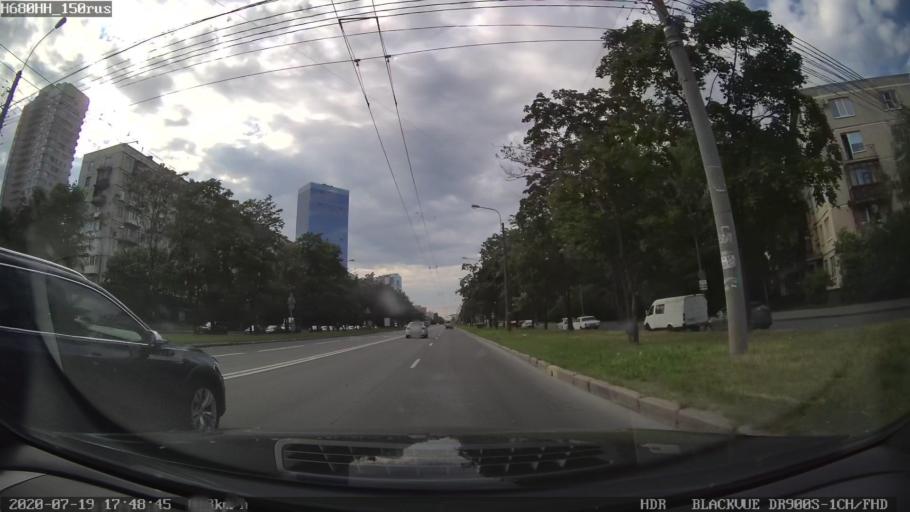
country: RU
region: St.-Petersburg
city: Kupchino
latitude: 59.8485
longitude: 30.3113
